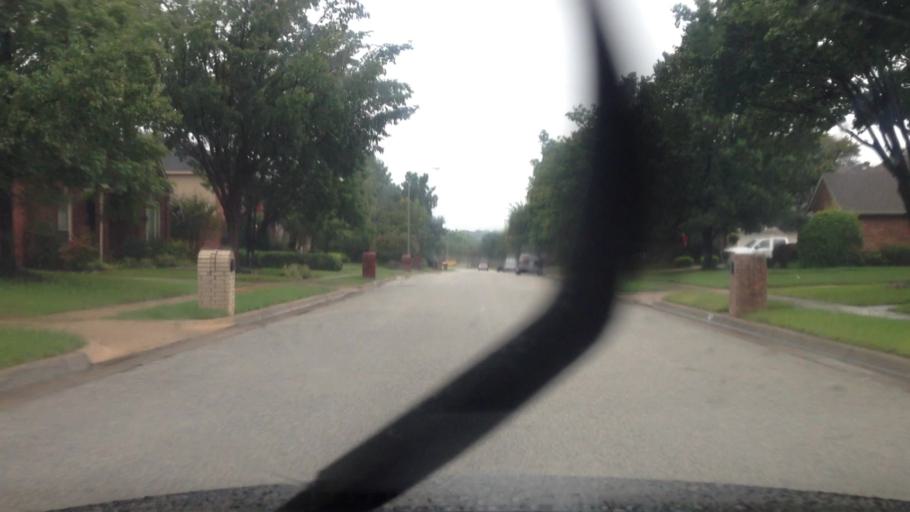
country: US
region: Texas
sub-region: Tarrant County
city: Keller
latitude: 32.9041
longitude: -97.2082
